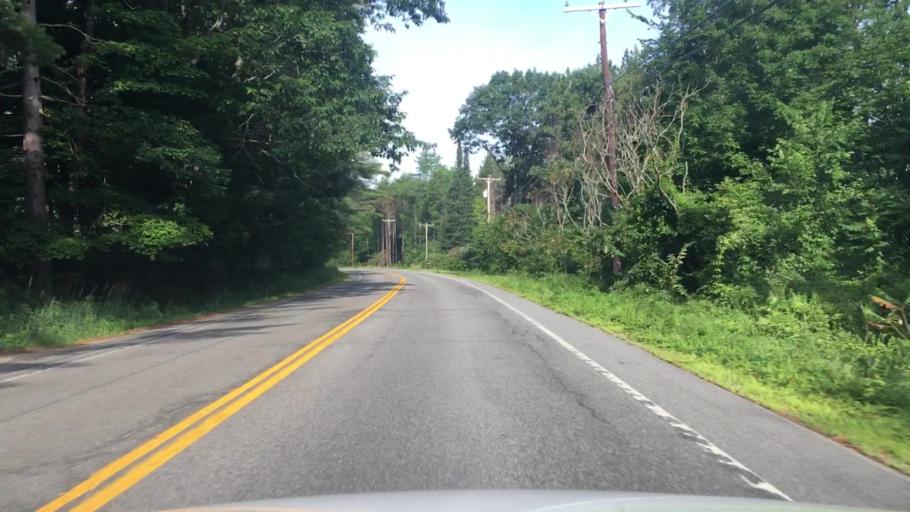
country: US
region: Maine
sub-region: York County
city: Cornish
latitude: 43.8061
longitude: -70.8378
